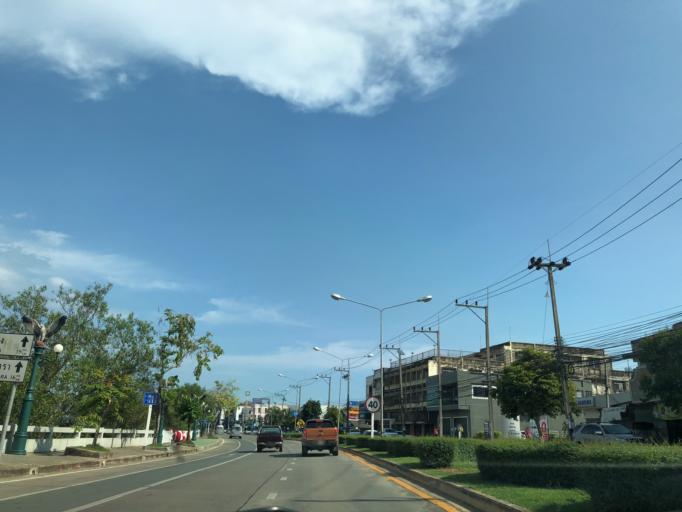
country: TH
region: Krabi
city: Krabi
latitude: 8.0694
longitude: 98.9167
